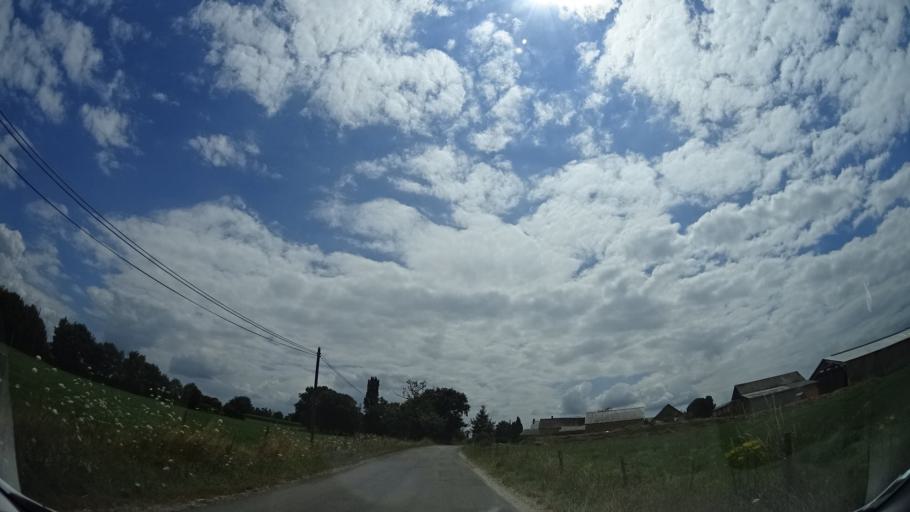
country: FR
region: Brittany
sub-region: Departement d'Ille-et-Vilaine
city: La Meziere
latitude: 48.1997
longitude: -1.7578
